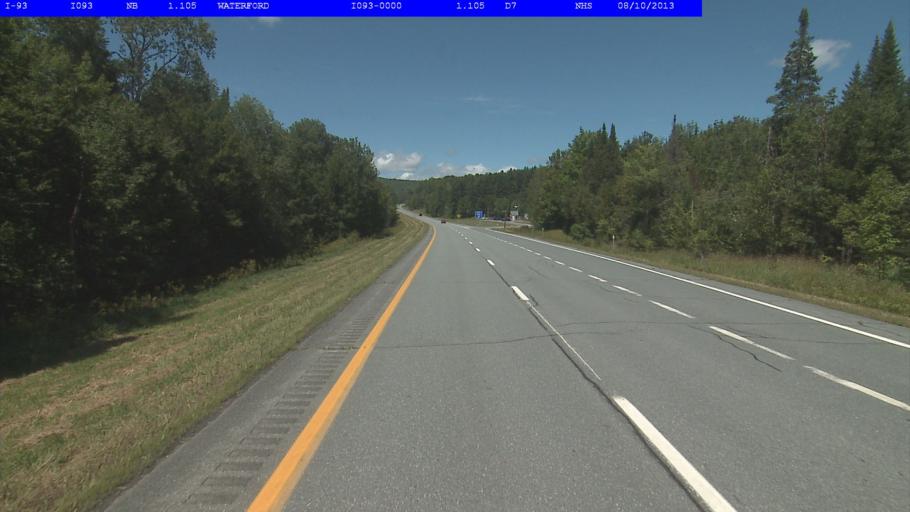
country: US
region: Vermont
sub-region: Caledonia County
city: Saint Johnsbury
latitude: 44.3585
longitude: -71.8971
